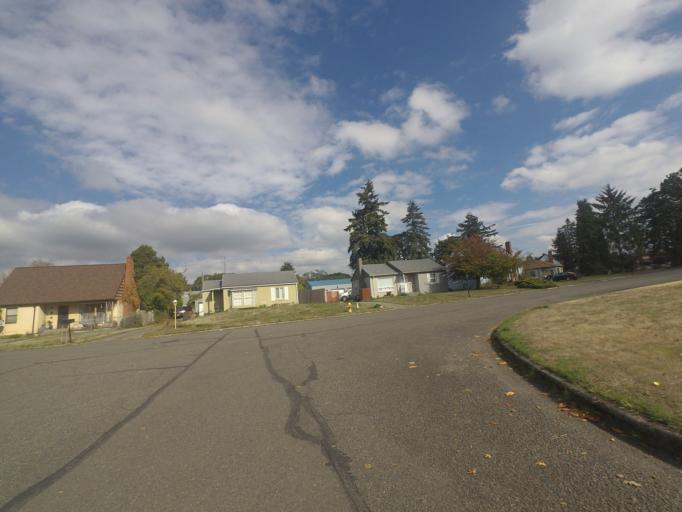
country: US
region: Washington
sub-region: Pierce County
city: Lakewood
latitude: 47.1675
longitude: -122.5136
